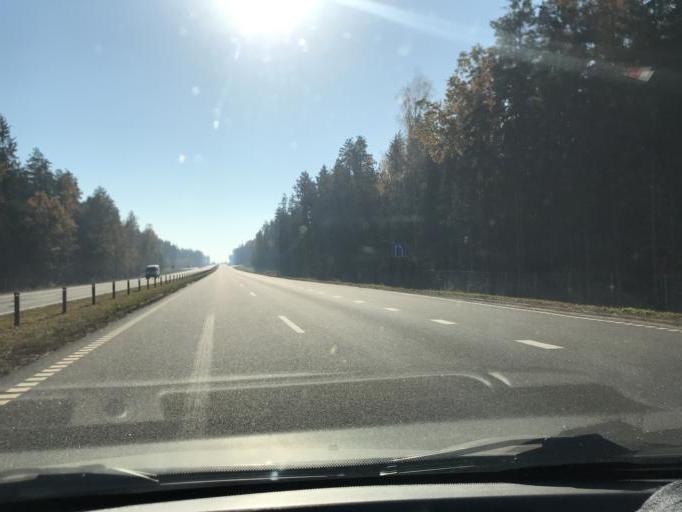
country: BY
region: Mogilev
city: Babruysk
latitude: 53.2080
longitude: 29.3459
